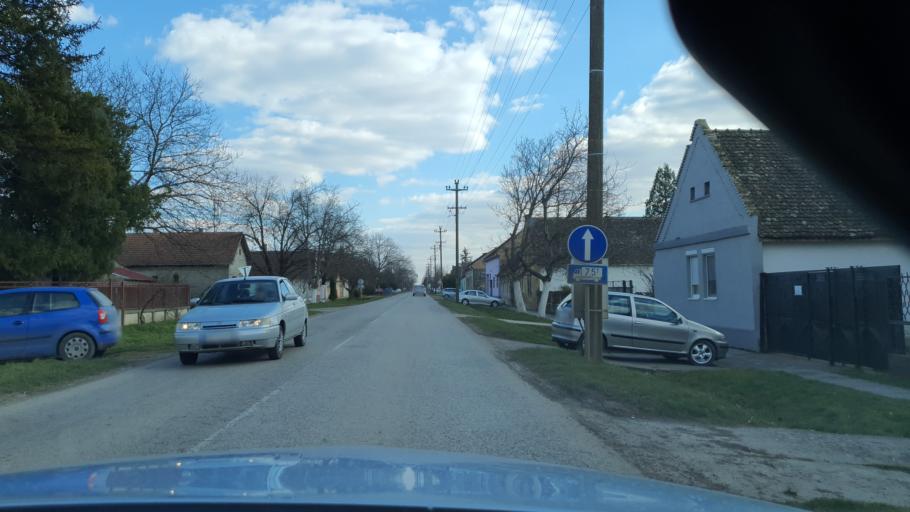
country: RS
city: Ravno Selo
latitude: 45.4511
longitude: 19.6183
